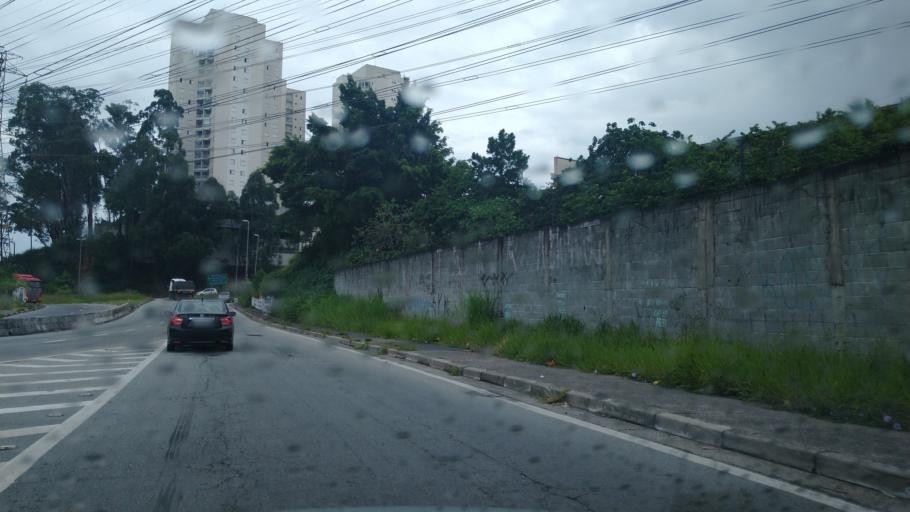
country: BR
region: Sao Paulo
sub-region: Guarulhos
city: Guarulhos
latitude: -23.4865
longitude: -46.5583
